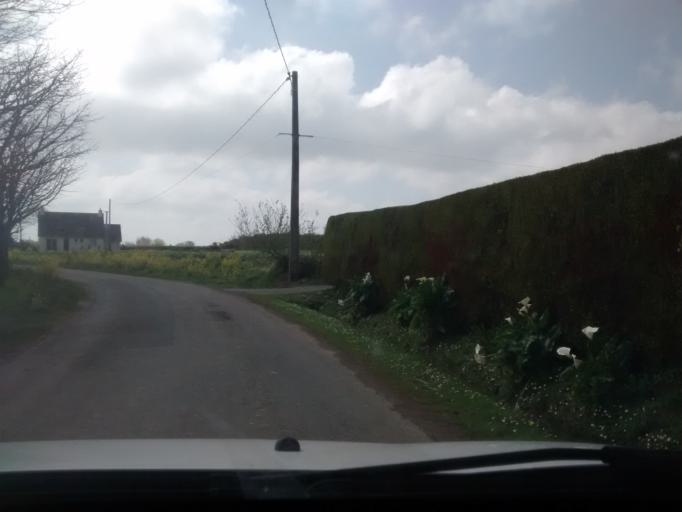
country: FR
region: Brittany
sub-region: Departement des Cotes-d'Armor
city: Penvenan
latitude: 48.8112
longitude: -3.3050
